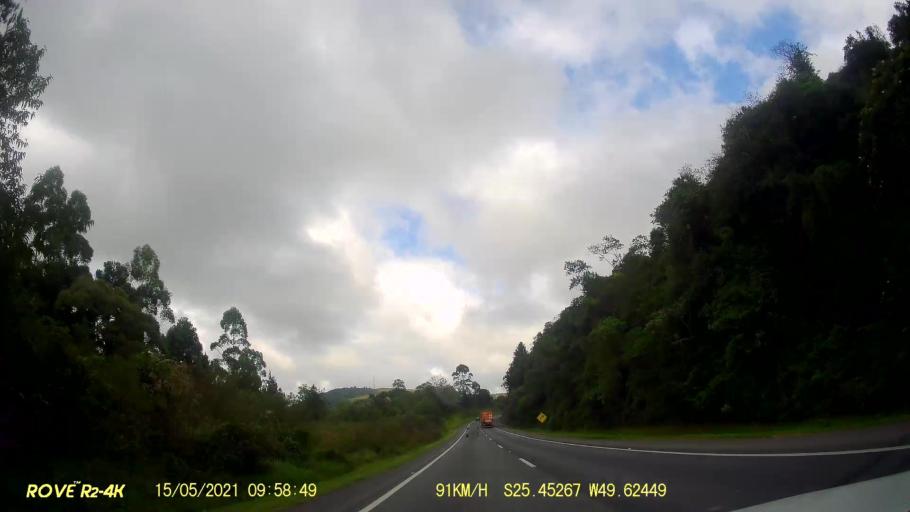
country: BR
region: Parana
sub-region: Campo Largo
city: Campo Largo
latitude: -25.4527
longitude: -49.6245
